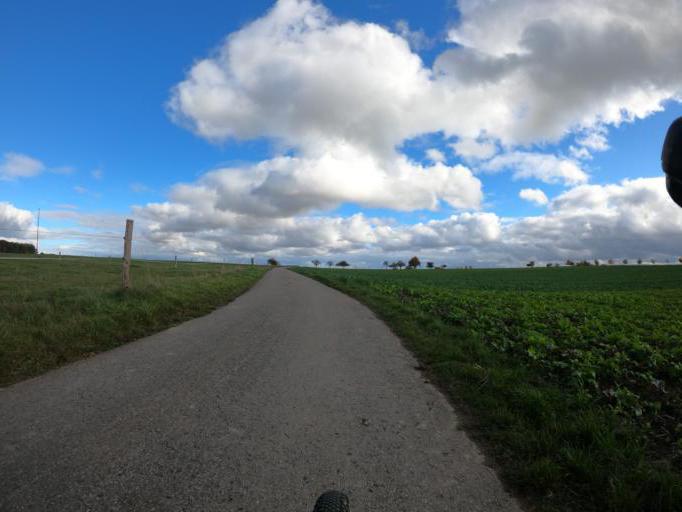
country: DE
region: Baden-Wuerttemberg
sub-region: Regierungsbezirk Stuttgart
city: Magstadt
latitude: 48.7199
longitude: 8.9282
